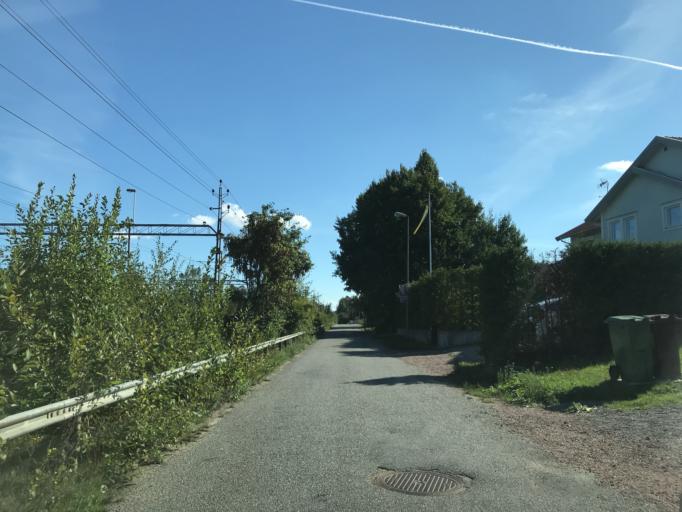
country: SE
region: Stockholm
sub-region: Sollentuna Kommun
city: Sollentuna
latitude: 59.4188
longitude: 17.9554
